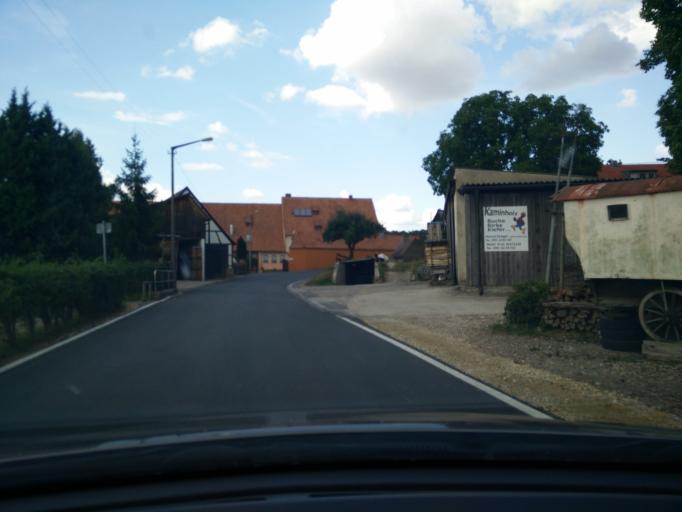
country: DE
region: Bavaria
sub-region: Regierungsbezirk Mittelfranken
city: Stein
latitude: 49.3895
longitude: 11.0294
